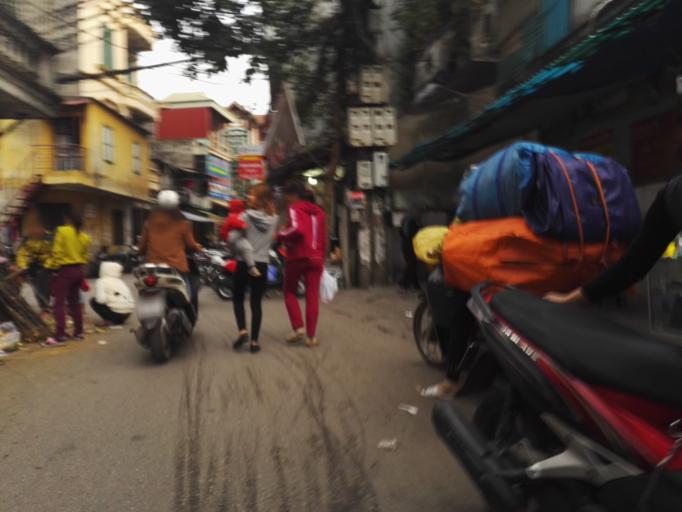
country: VN
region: Ha Noi
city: Hoan Kiem
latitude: 21.0430
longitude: 105.8508
